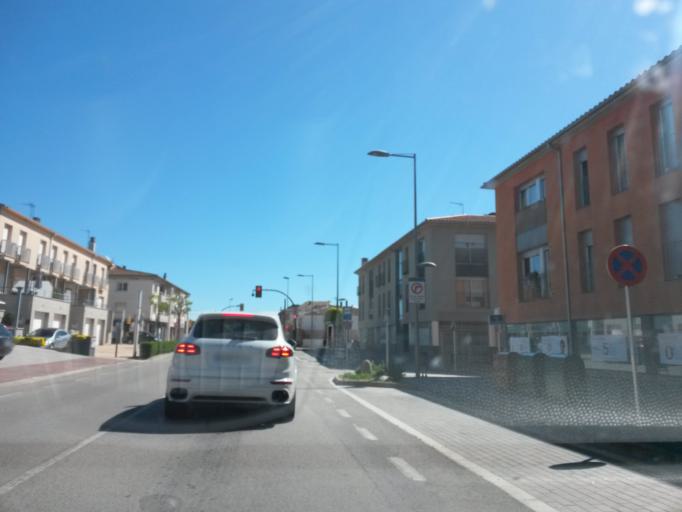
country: ES
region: Catalonia
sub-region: Provincia de Girona
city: Riudellots de la Selva
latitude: 41.8943
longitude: 2.8035
